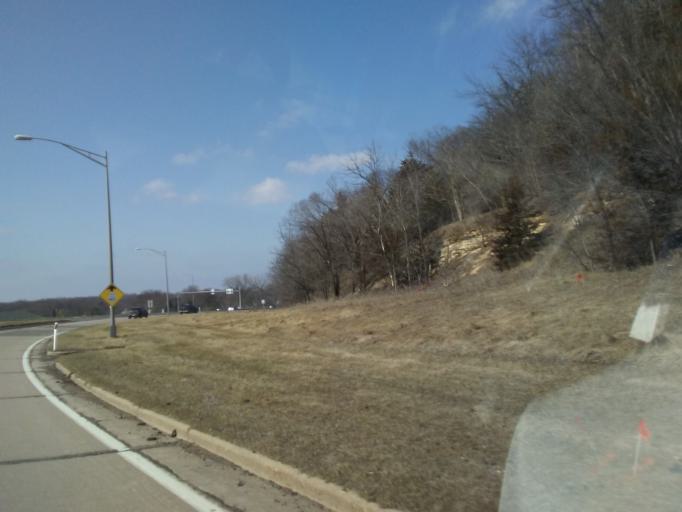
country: US
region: Wisconsin
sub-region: La Crosse County
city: La Crosse
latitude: 43.7523
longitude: -91.2006
